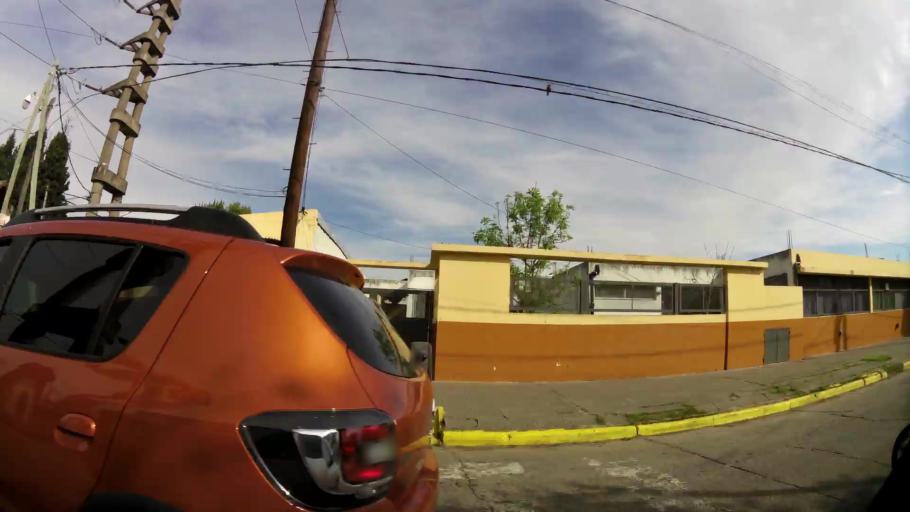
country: AR
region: Buenos Aires
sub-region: Partido de Quilmes
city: Quilmes
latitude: -34.7586
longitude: -58.2725
